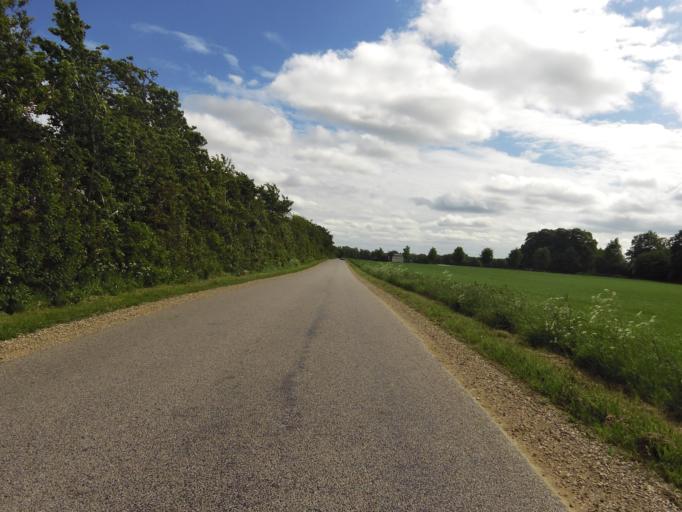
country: DK
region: South Denmark
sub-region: Vejen Kommune
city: Vejen
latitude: 55.4422
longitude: 9.1090
